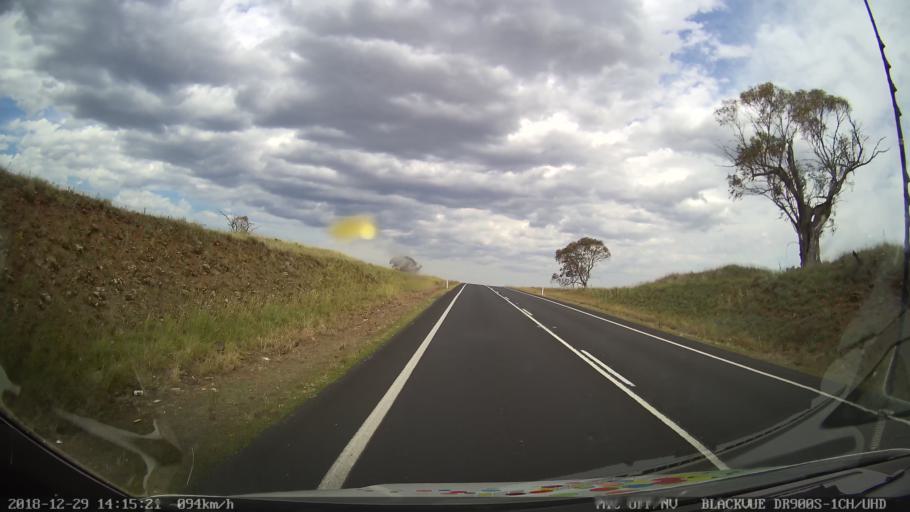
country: AU
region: New South Wales
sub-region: Cooma-Monaro
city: Cooma
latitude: -36.4547
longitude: 149.2397
